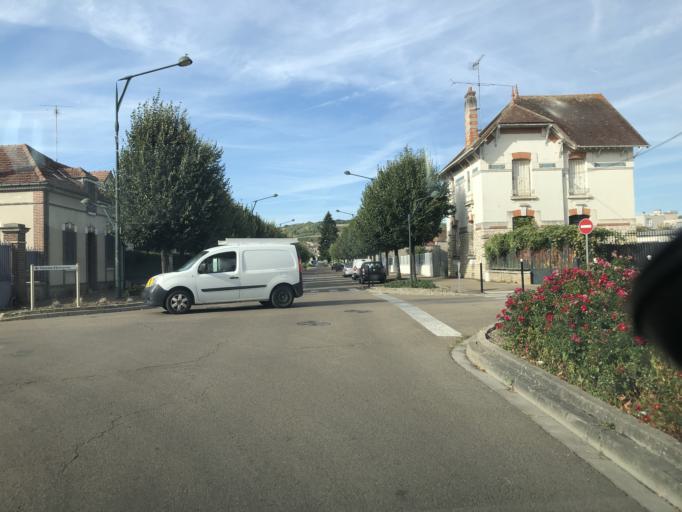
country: FR
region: Bourgogne
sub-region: Departement de l'Yonne
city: Joigny
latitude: 47.9751
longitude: 3.3934
